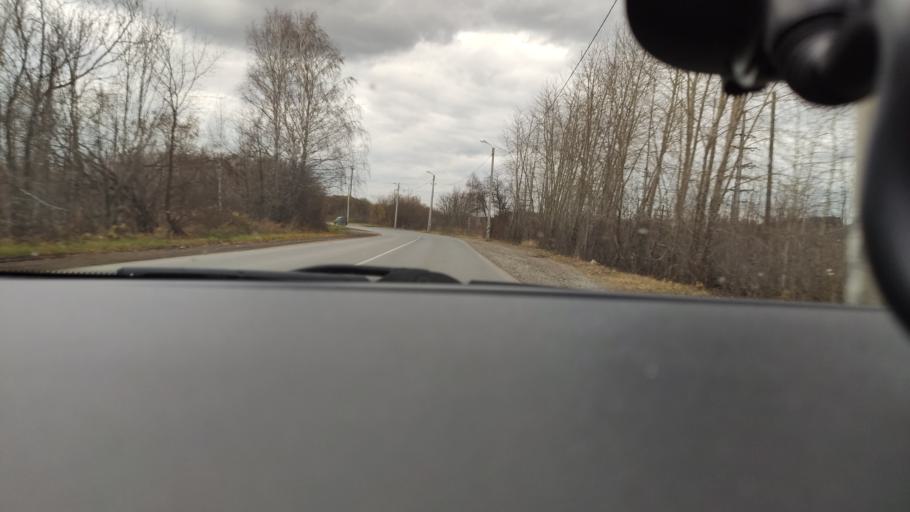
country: RU
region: Perm
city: Kondratovo
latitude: 57.9437
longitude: 56.1534
